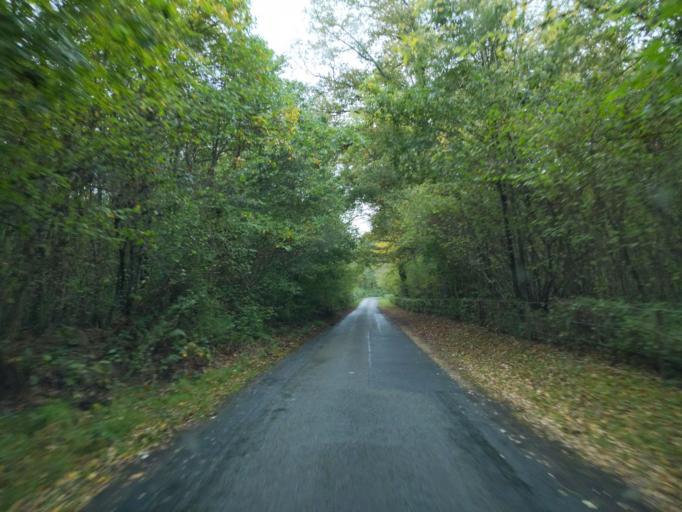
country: FR
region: Ile-de-France
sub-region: Departement des Yvelines
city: Bullion
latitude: 48.6087
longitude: 1.9807
